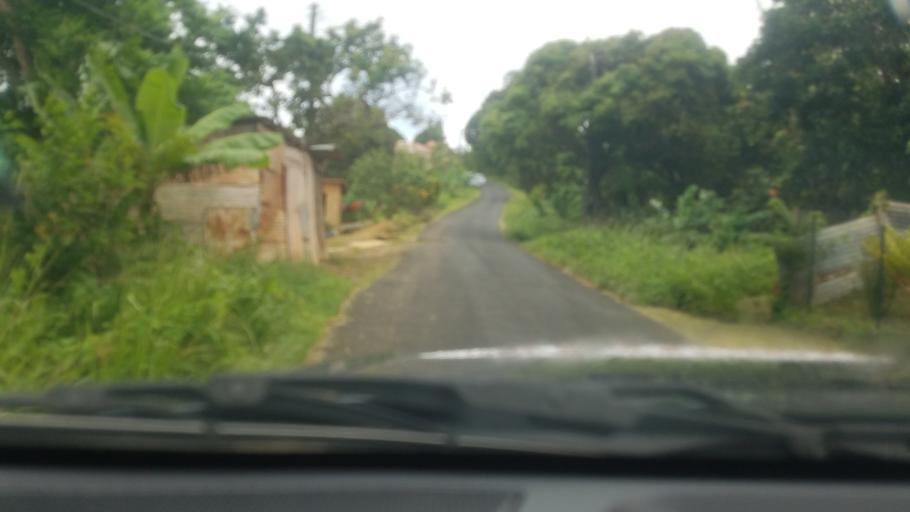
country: LC
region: Micoud Quarter
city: Micoud
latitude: 13.8097
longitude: -60.9514
